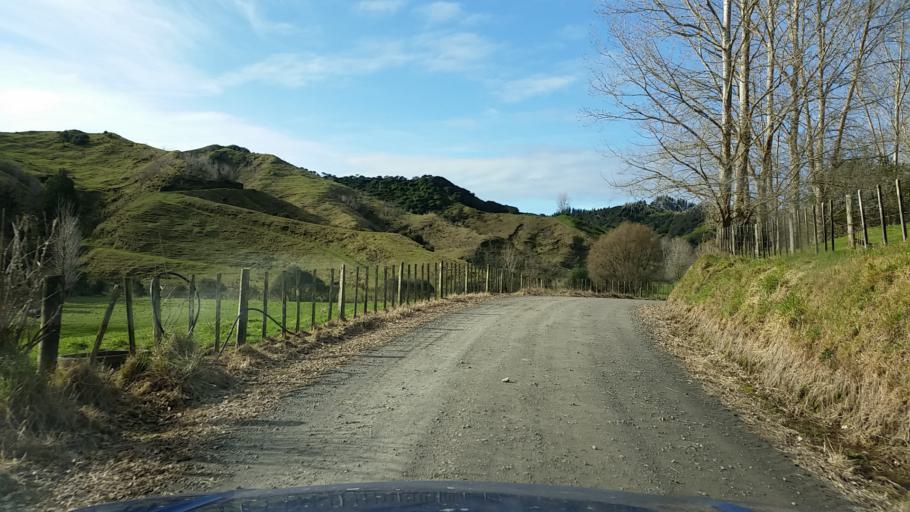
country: NZ
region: Taranaki
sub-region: South Taranaki District
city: Eltham
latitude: -39.2605
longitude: 174.5844
